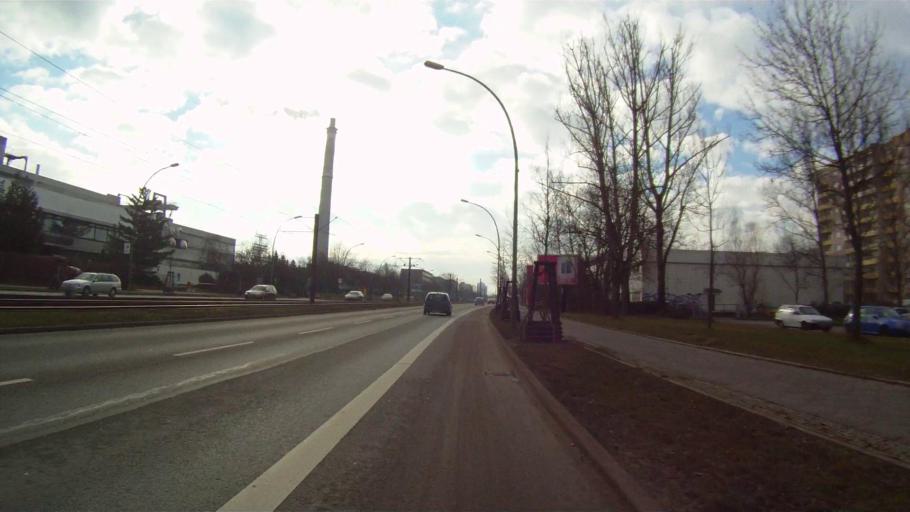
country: DE
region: Berlin
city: Friedrichsfelde
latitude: 52.5249
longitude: 13.5197
